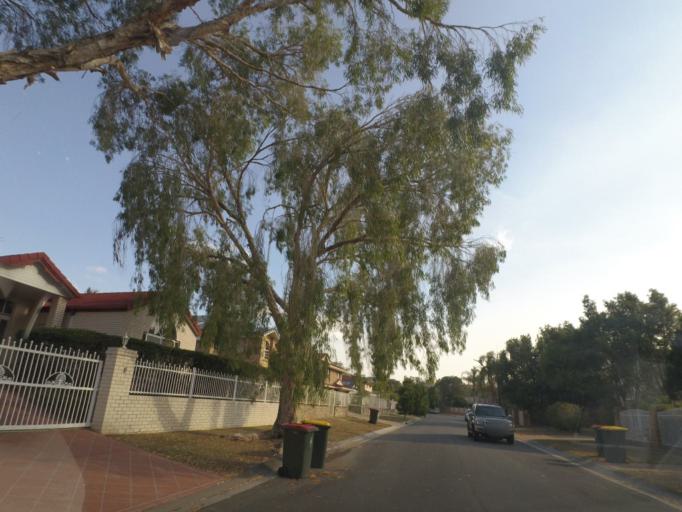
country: AU
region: Queensland
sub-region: Brisbane
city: Robertson
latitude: -27.5602
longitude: 153.0562
